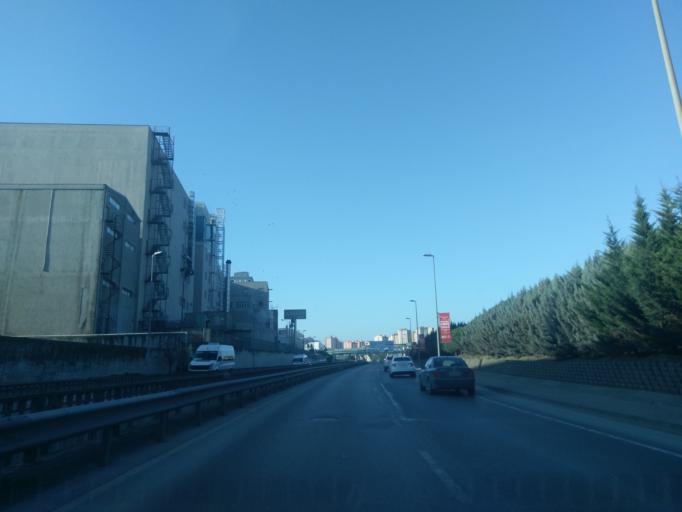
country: TR
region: Istanbul
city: Basaksehir
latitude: 41.0776
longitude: 28.8129
